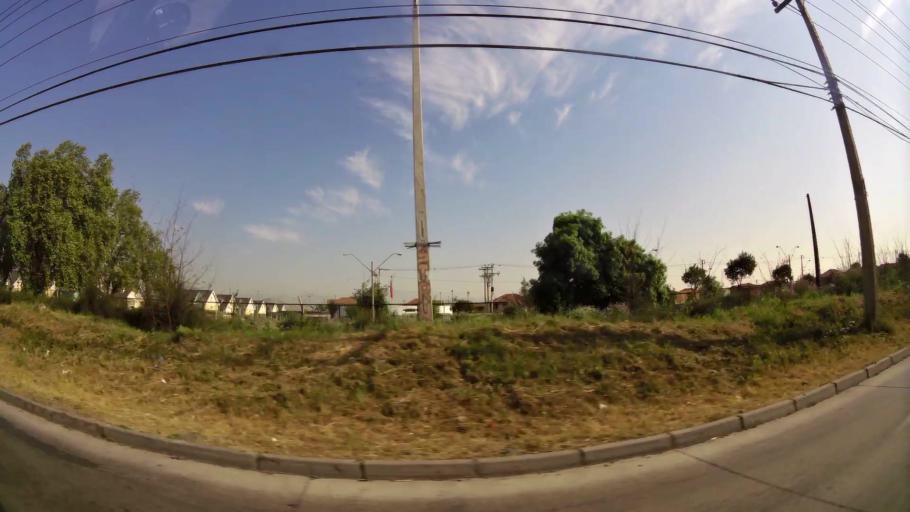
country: CL
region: Santiago Metropolitan
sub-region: Provincia de Maipo
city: San Bernardo
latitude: -33.5472
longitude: -70.7861
